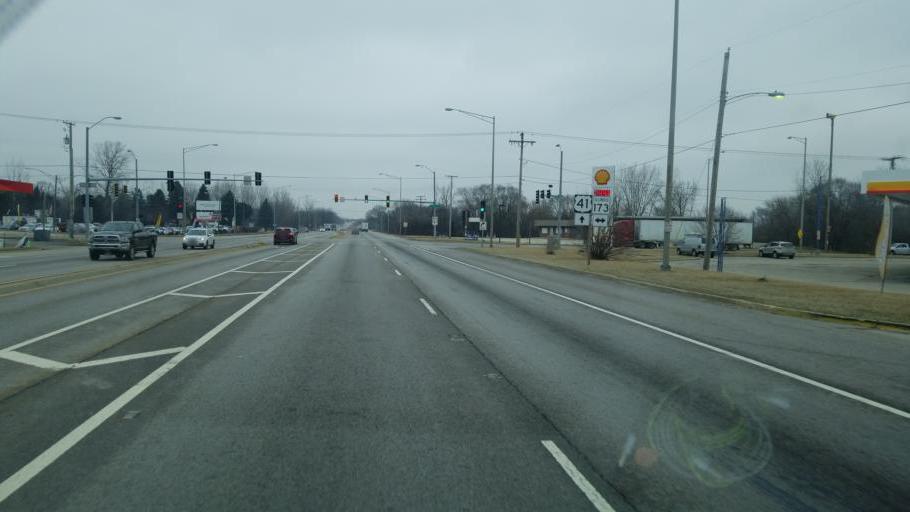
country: US
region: Illinois
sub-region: Lake County
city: Wadsworth
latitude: 42.4645
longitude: -87.9464
